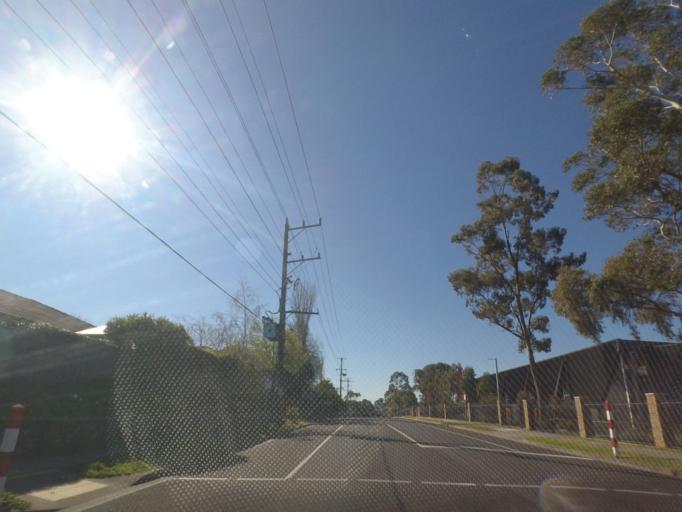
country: AU
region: Victoria
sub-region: Maroondah
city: Croydon Hills
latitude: -37.7836
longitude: 145.2558
